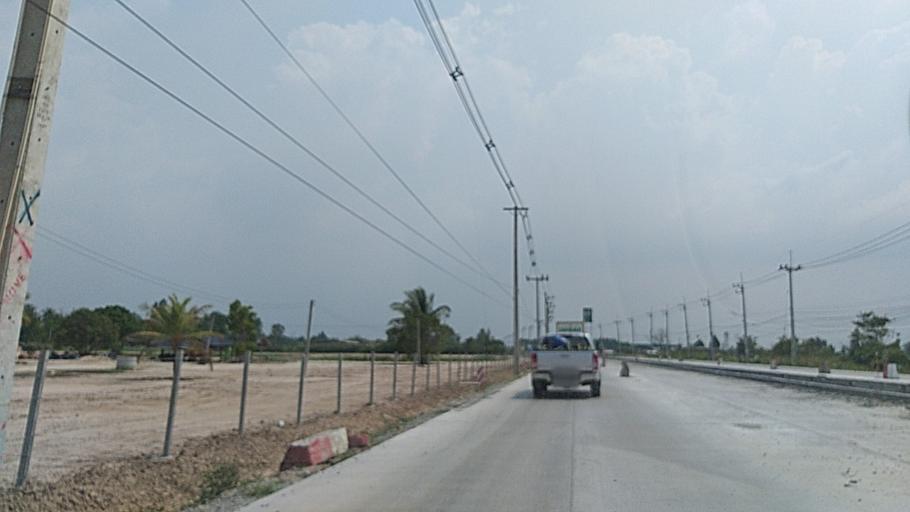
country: TH
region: Chon Buri
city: Phanat Nikhom
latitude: 13.3839
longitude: 101.1935
